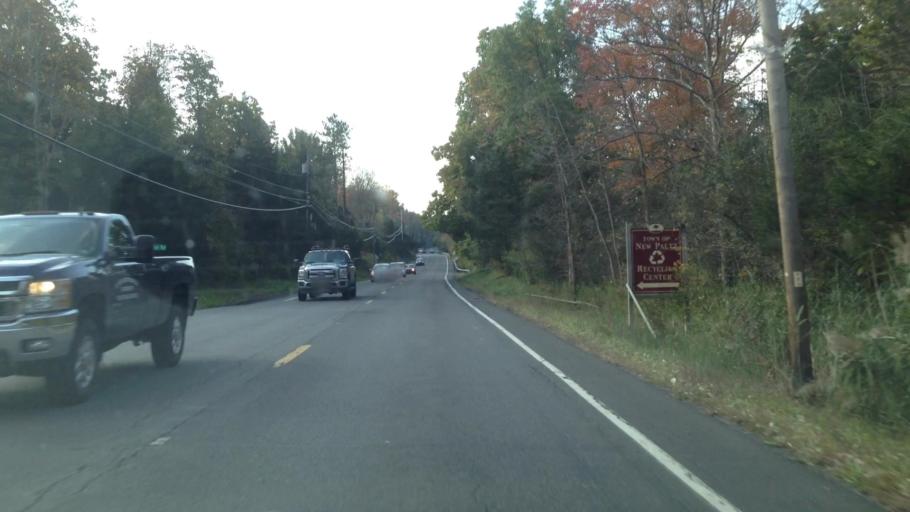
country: US
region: New York
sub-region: Ulster County
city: Tillson
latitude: 41.7916
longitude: -74.0686
